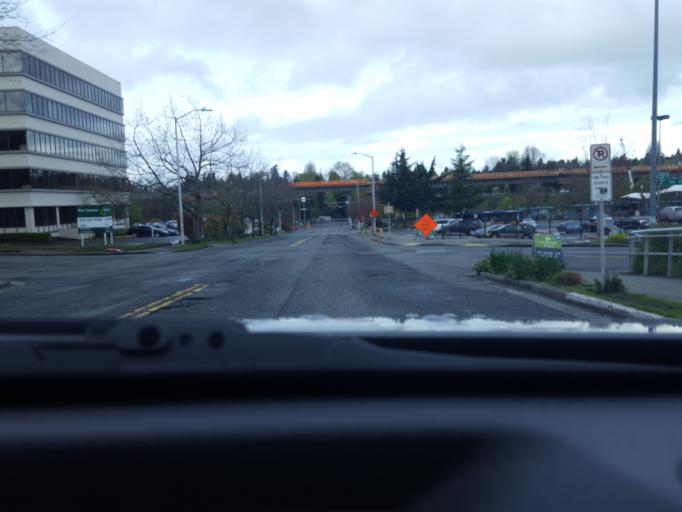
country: US
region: Washington
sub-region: King County
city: Shoreline
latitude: 47.7014
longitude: -122.3253
